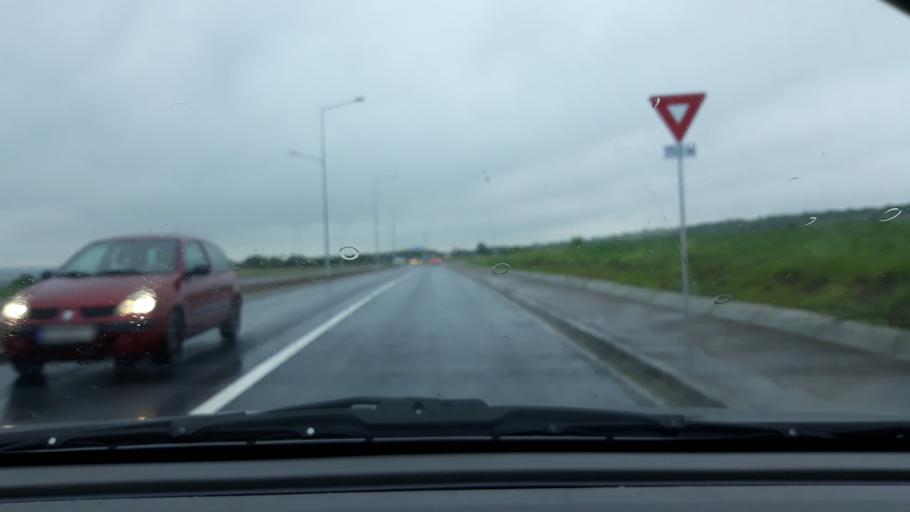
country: RO
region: Bihor
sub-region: Comuna Biharea
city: Biharea
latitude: 47.1074
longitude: 21.9067
